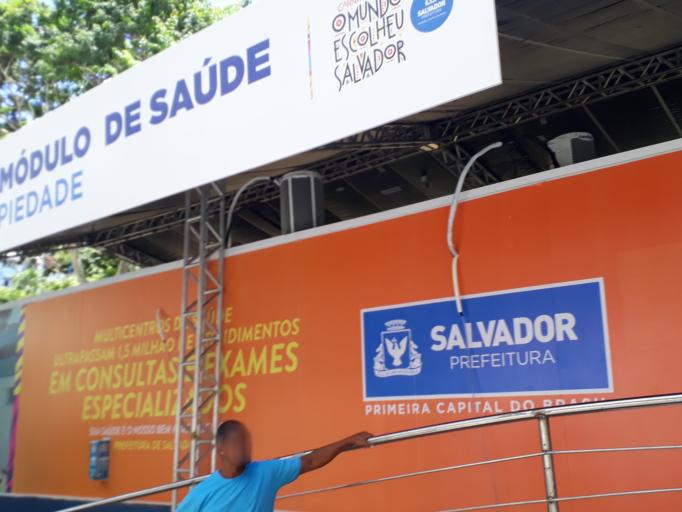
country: BR
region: Bahia
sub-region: Salvador
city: Salvador
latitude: -12.9837
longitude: -38.5152
